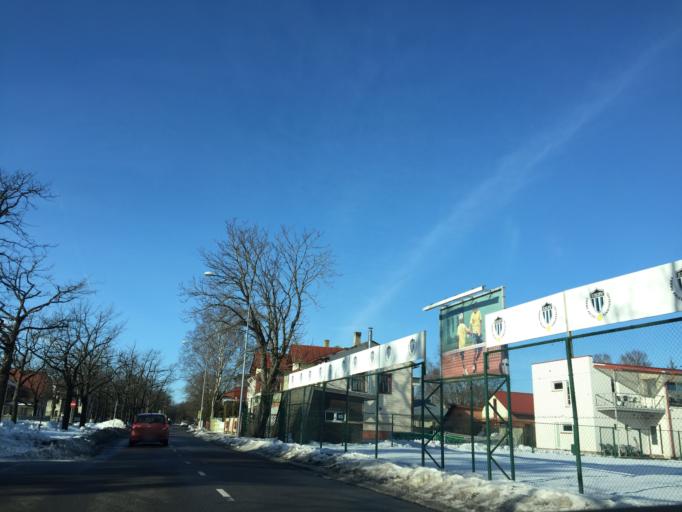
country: EE
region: Paernumaa
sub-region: Paernu linn
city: Parnu
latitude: 58.3760
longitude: 24.5065
